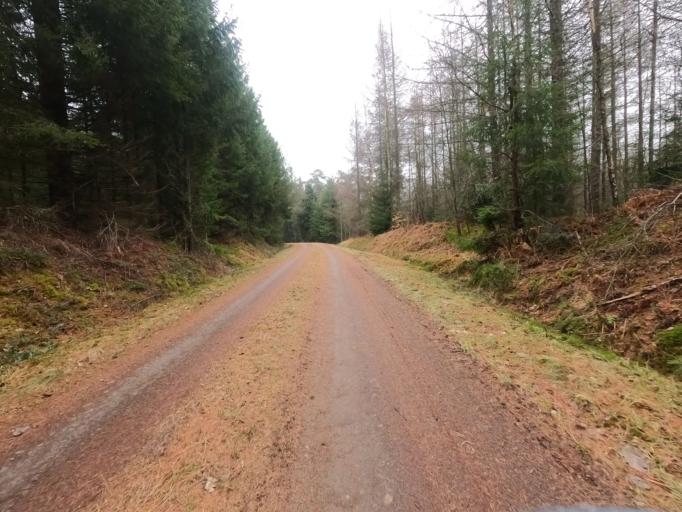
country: SE
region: Kronoberg
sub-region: Markaryds Kommun
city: Stromsnasbruk
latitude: 56.7895
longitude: 13.6298
